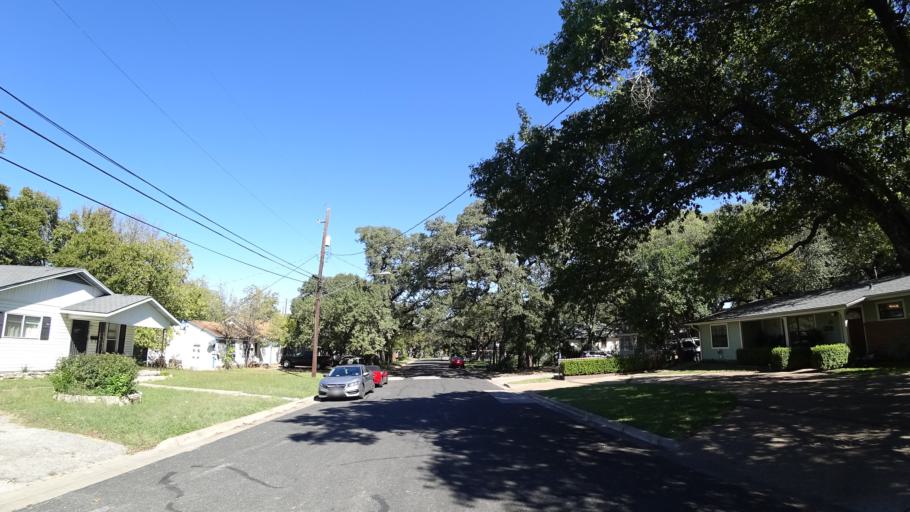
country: US
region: Texas
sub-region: Travis County
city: Austin
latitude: 30.2398
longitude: -97.7651
